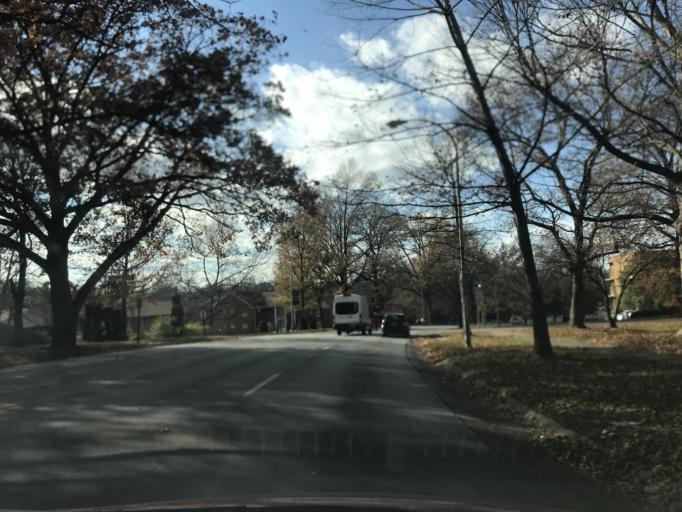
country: US
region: Kentucky
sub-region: Jefferson County
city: Audubon Park
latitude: 38.2253
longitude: -85.7239
